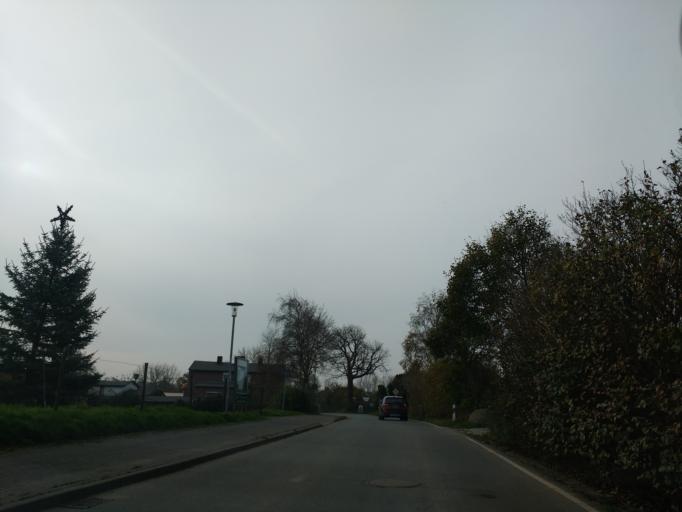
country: DE
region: Mecklenburg-Vorpommern
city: Ostseebad Boltenhagen
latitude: 53.9956
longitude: 11.1859
